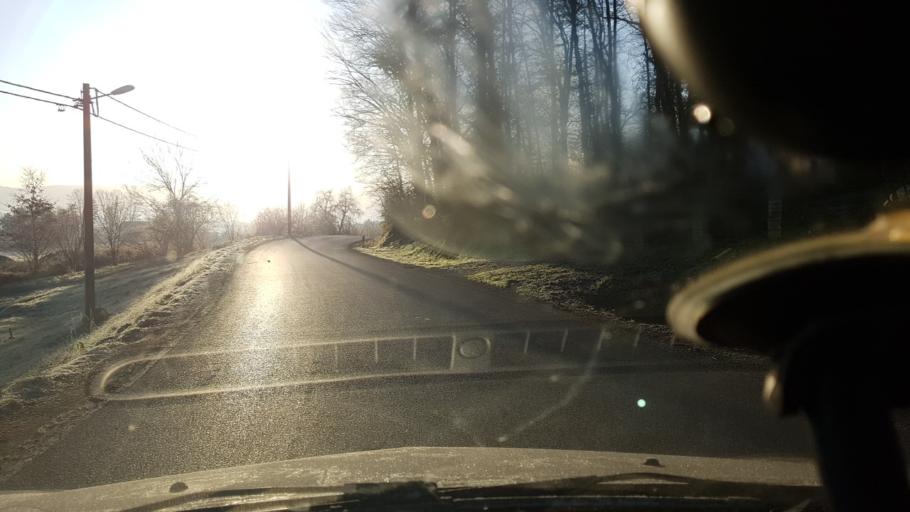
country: HR
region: Zagrebacka
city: Jakovlje
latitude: 45.9790
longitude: 15.8428
